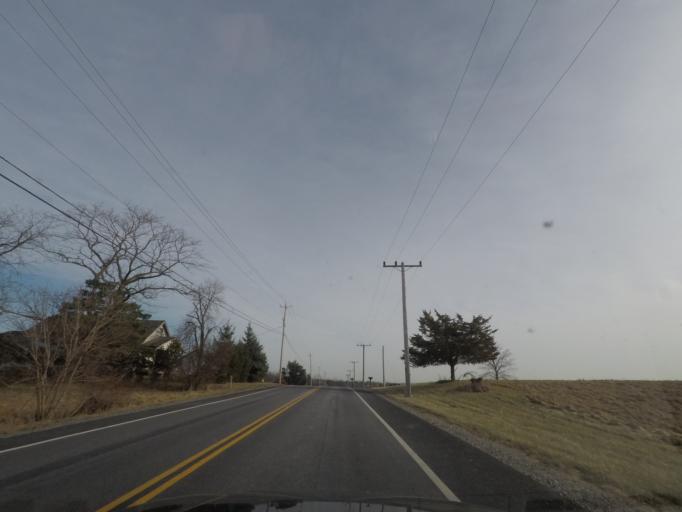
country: US
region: New York
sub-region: Saratoga County
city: Mechanicville
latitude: 42.8720
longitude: -73.7147
